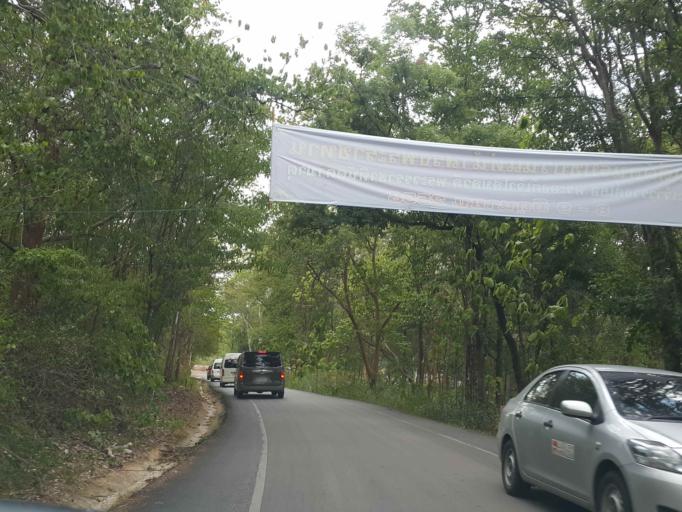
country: TH
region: Chiang Mai
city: Hang Dong
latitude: 18.7560
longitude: 98.9216
